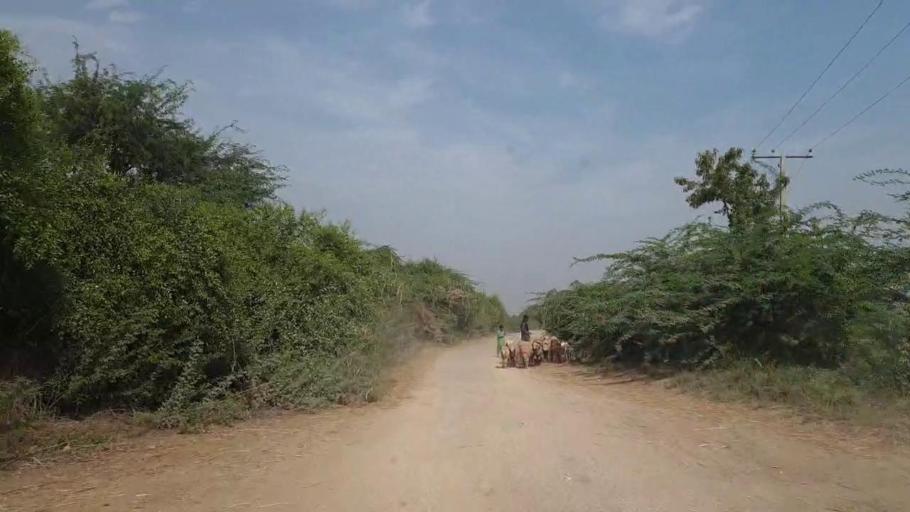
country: PK
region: Sindh
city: Tando Bago
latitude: 24.9266
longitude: 68.9877
